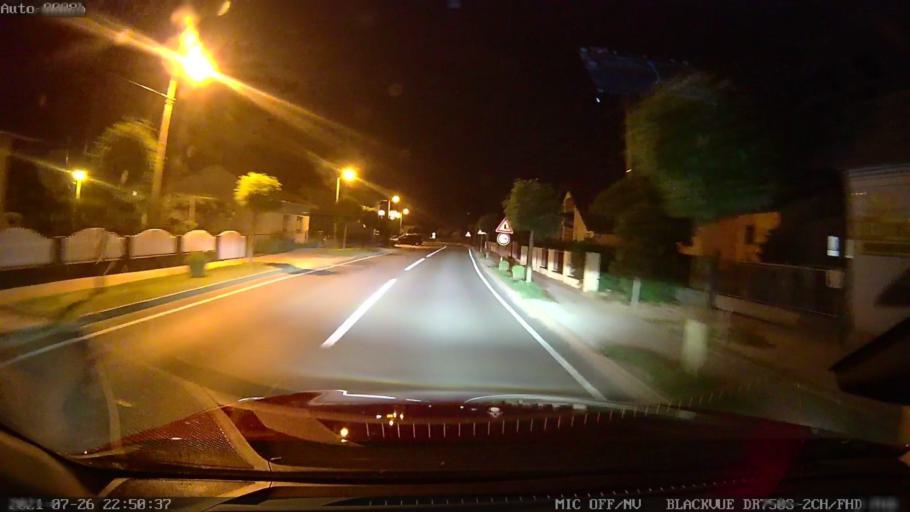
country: HR
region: Varazdinska
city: Jalkovec
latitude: 46.2563
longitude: 16.3671
